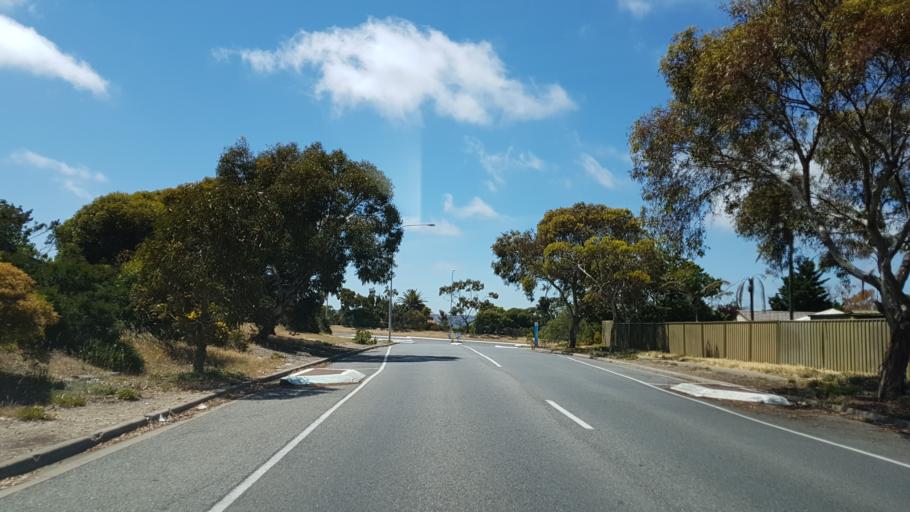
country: AU
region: South Australia
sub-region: Marion
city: Happy Valley
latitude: -35.0692
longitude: 138.5270
